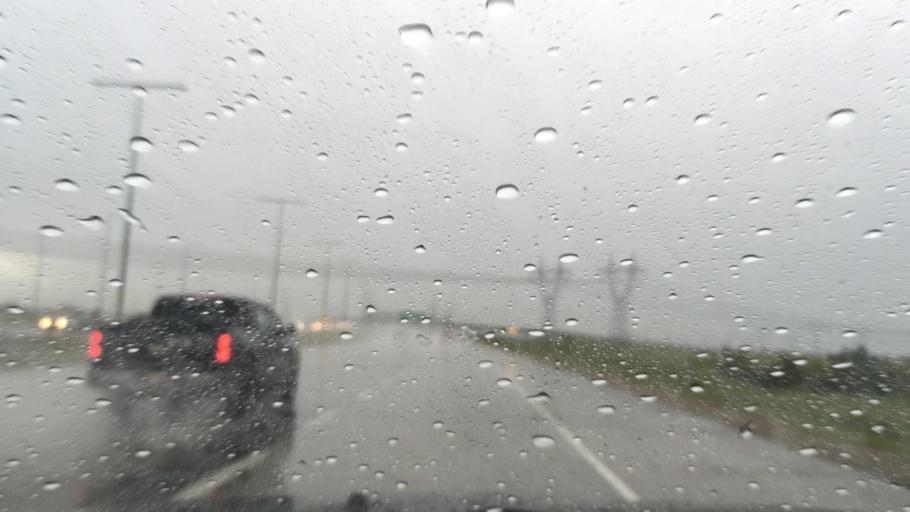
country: CA
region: Alberta
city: Edmonton
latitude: 53.4347
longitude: -113.5094
